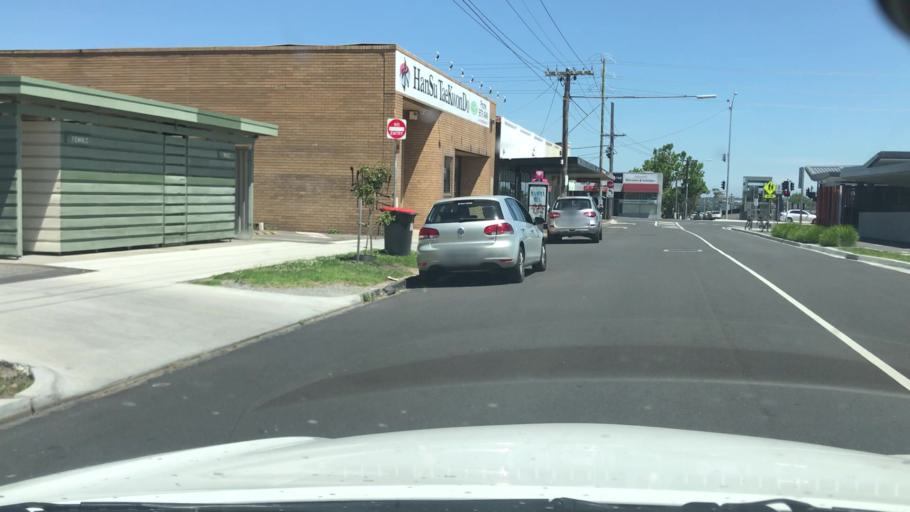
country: AU
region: Victoria
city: Ormond
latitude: -37.9030
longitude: 145.0400
